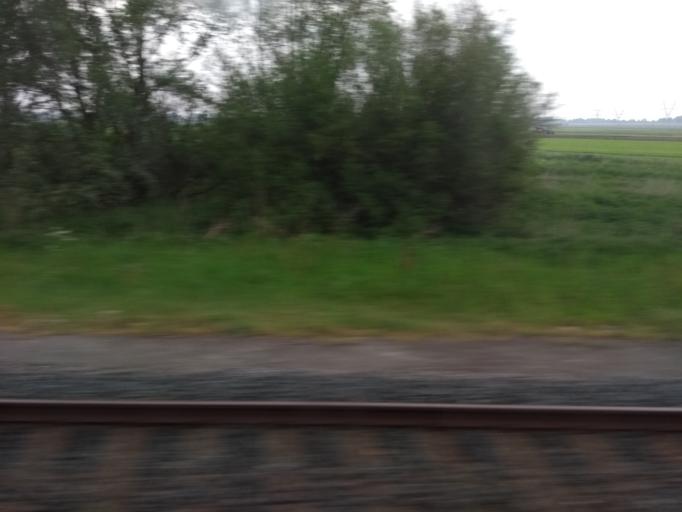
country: NL
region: North Holland
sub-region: Gemeente Weesp
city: Weesp
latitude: 52.3099
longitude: 5.0749
